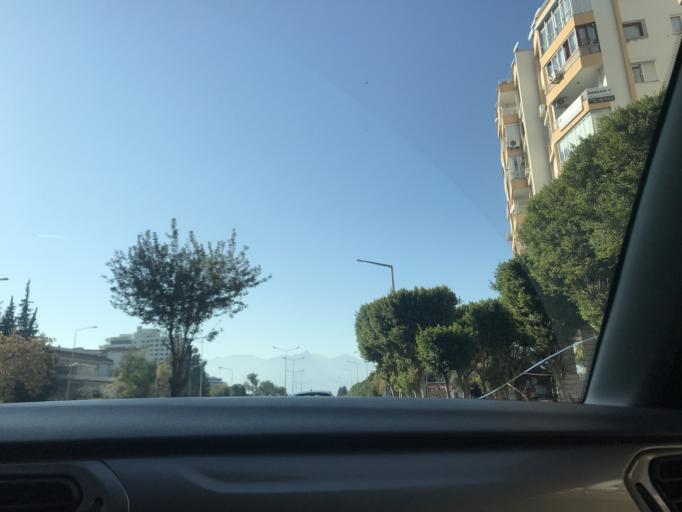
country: TR
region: Antalya
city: Antalya
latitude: 36.8885
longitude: 30.6804
